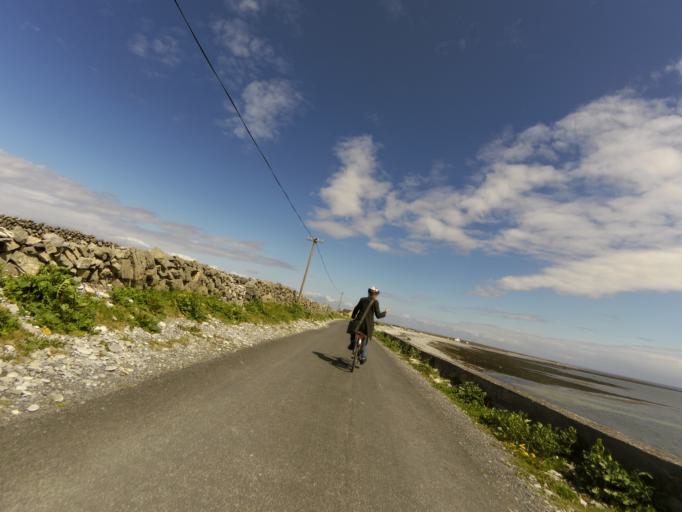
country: IE
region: Connaught
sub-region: County Galway
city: Oughterard
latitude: 53.1219
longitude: -9.6645
